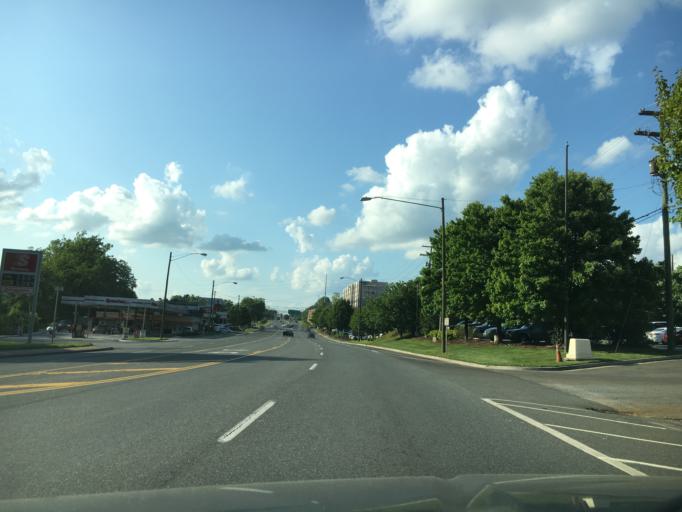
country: US
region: Virginia
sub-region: City of Lynchburg
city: West Lynchburg
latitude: 37.3589
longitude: -79.1807
